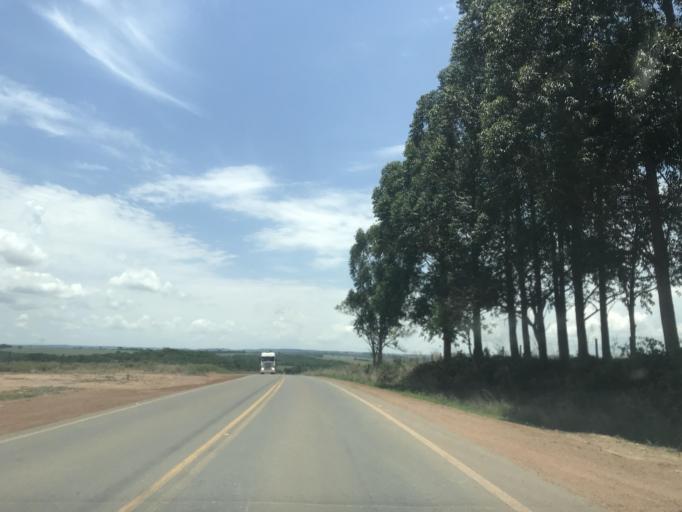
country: BR
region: Goias
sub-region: Vianopolis
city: Vianopolis
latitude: -16.6310
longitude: -48.3555
